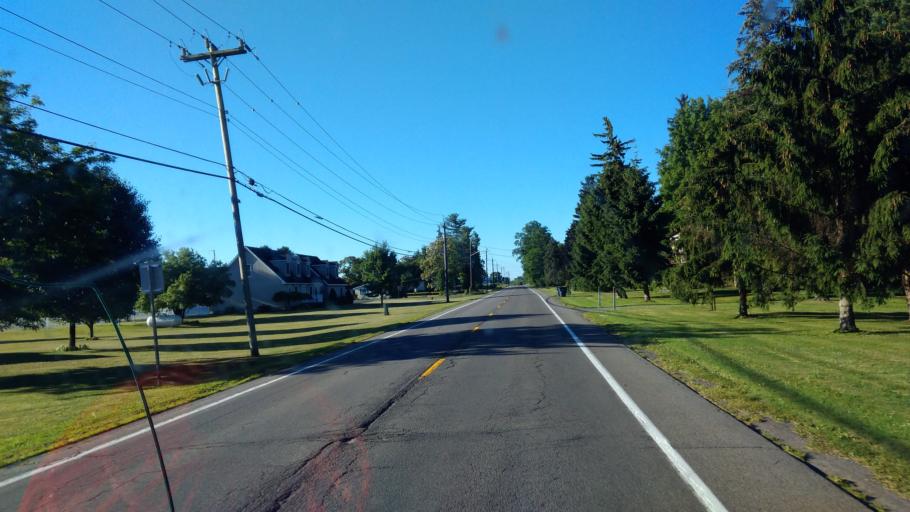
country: US
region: New York
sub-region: Wayne County
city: Lyons
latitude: 43.0459
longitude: -76.9939
